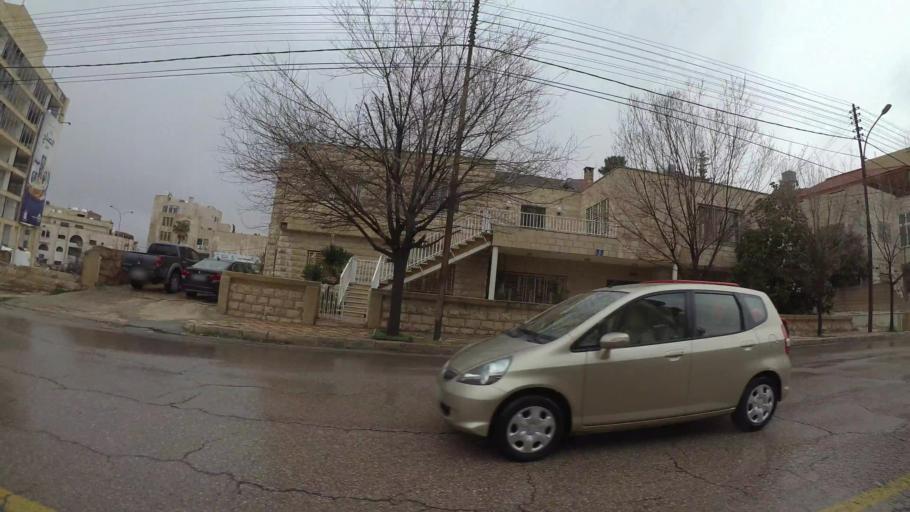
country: JO
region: Amman
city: Wadi as Sir
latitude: 31.9674
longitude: 35.8559
